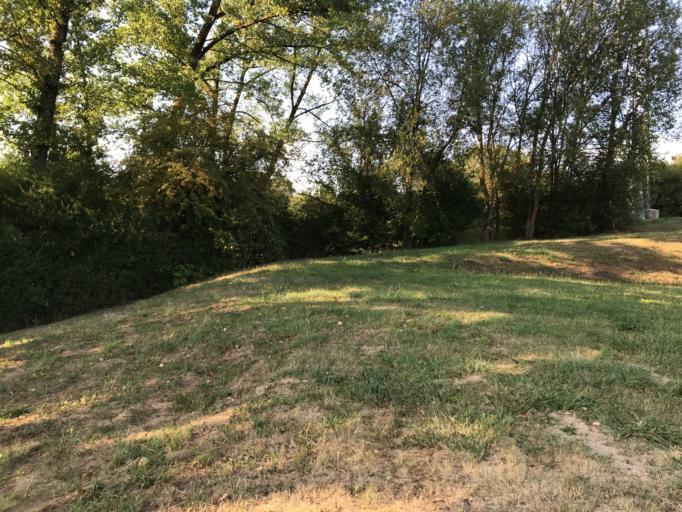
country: LU
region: Luxembourg
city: Soleuvre
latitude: 49.5108
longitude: 5.9462
